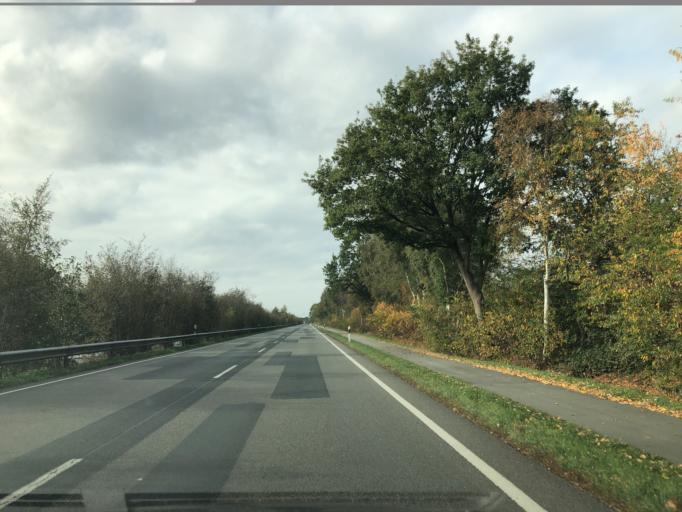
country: DE
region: Lower Saxony
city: Friesoythe
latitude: 53.0899
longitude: 7.8586
